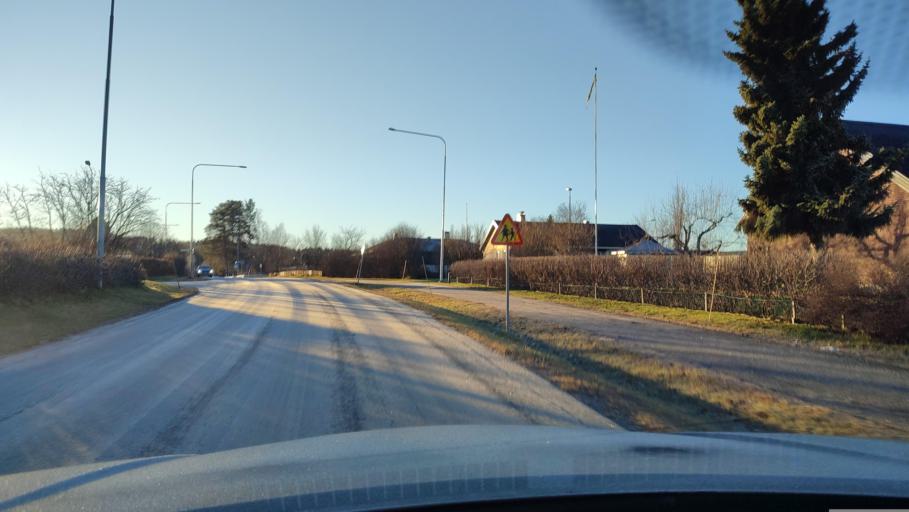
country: SE
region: Vaesterbotten
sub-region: Skelleftea Kommun
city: Viken
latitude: 64.7456
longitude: 20.9197
